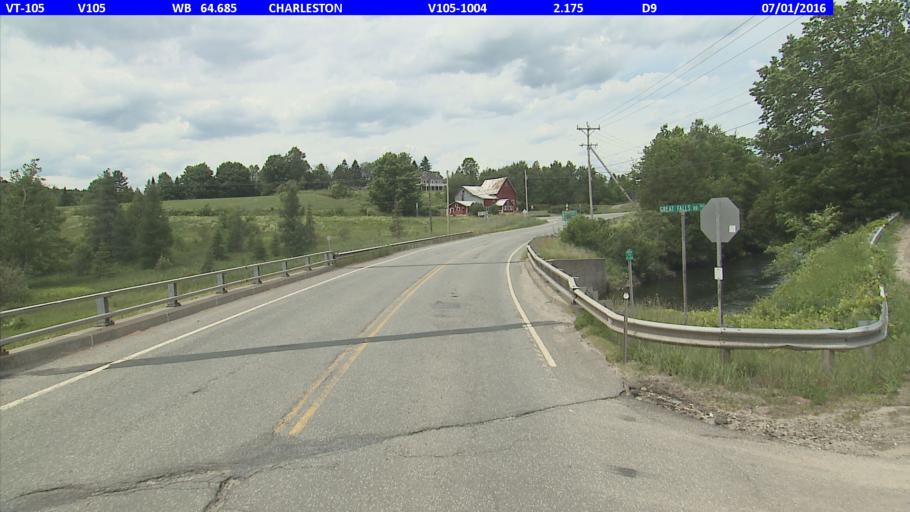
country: US
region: Vermont
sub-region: Orleans County
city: Newport
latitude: 44.8840
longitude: -72.0552
